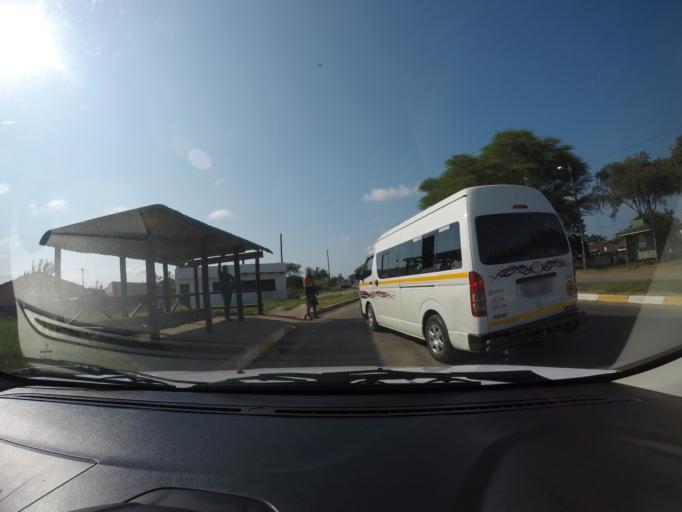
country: ZA
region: KwaZulu-Natal
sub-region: uThungulu District Municipality
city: eSikhawini
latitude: -28.8590
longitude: 31.9240
